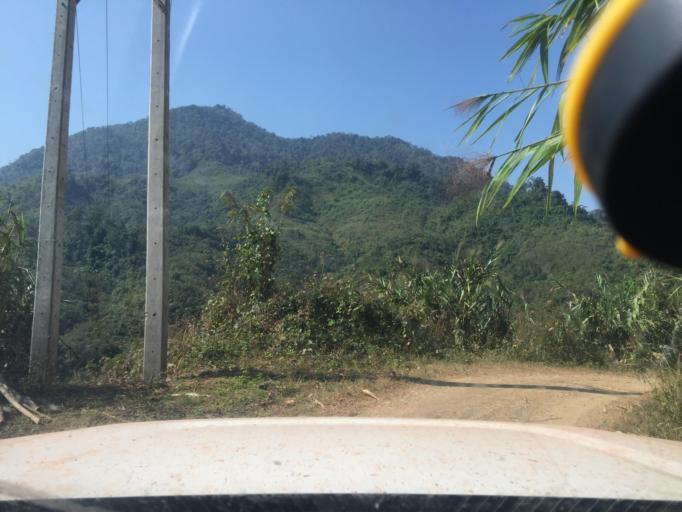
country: LA
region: Phongsali
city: Phongsali
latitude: 21.6476
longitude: 102.4090
